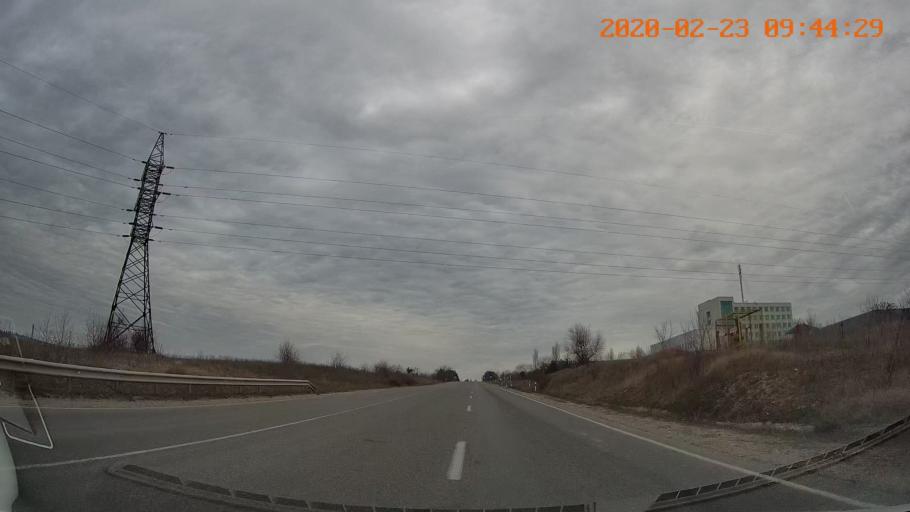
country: MD
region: Orhei
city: Orhei
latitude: 47.3967
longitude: 28.8011
